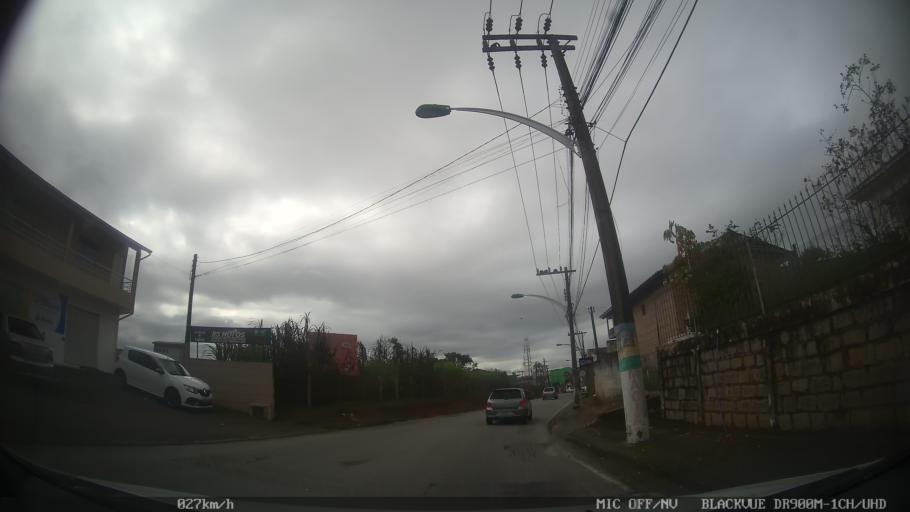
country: BR
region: Santa Catarina
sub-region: Biguacu
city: Biguacu
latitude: -27.5325
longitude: -48.6381
